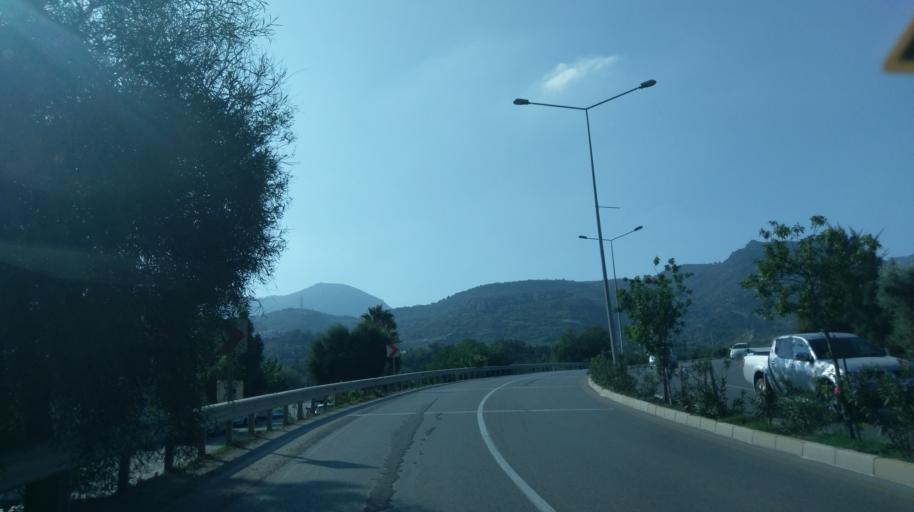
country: CY
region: Keryneia
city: Kyrenia
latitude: 35.3263
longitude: 33.3188
